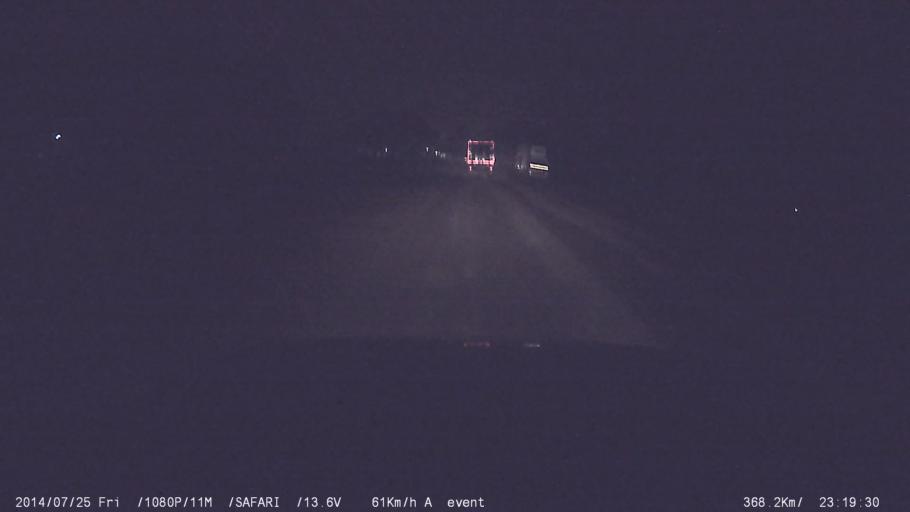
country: IN
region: Tamil Nadu
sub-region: Coimbatore
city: Madukkarai
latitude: 10.8817
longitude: 76.9065
